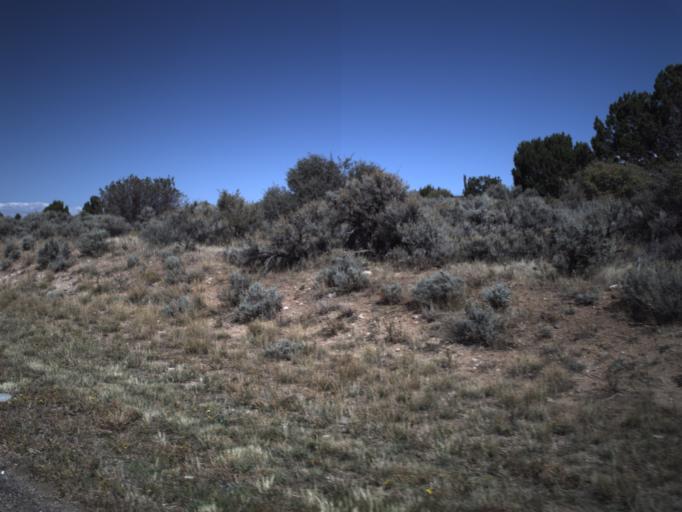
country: US
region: Utah
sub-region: Washington County
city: Enterprise
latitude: 37.4916
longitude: -113.6303
